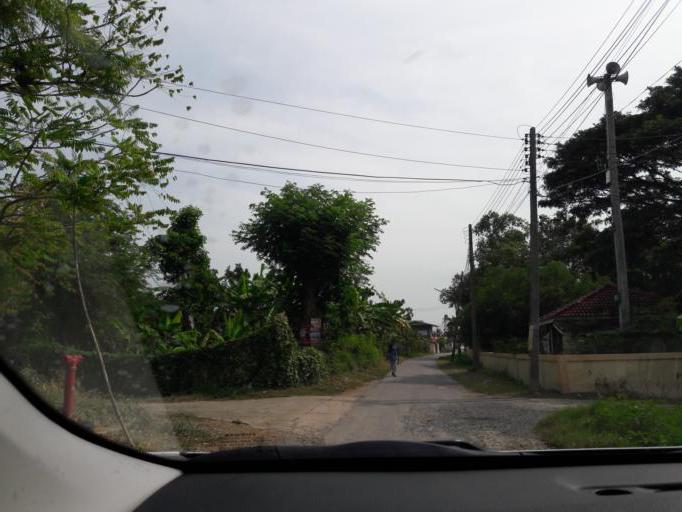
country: TH
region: Ang Thong
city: Ang Thong
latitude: 14.5902
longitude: 100.4672
